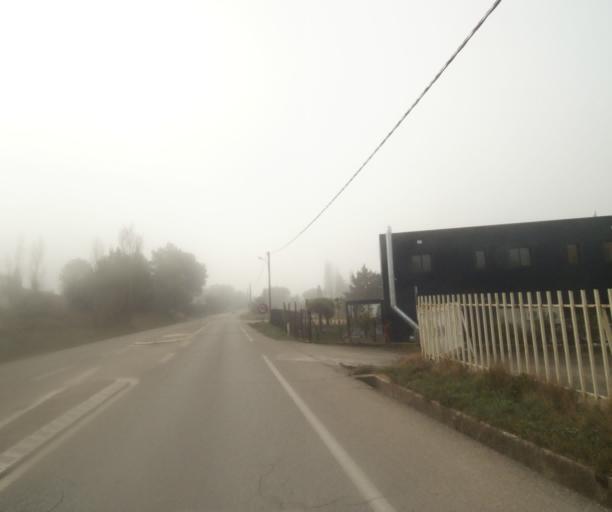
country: FR
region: Provence-Alpes-Cote d'Azur
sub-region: Departement des Bouches-du-Rhone
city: Eguilles
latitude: 43.5456
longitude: 5.3676
